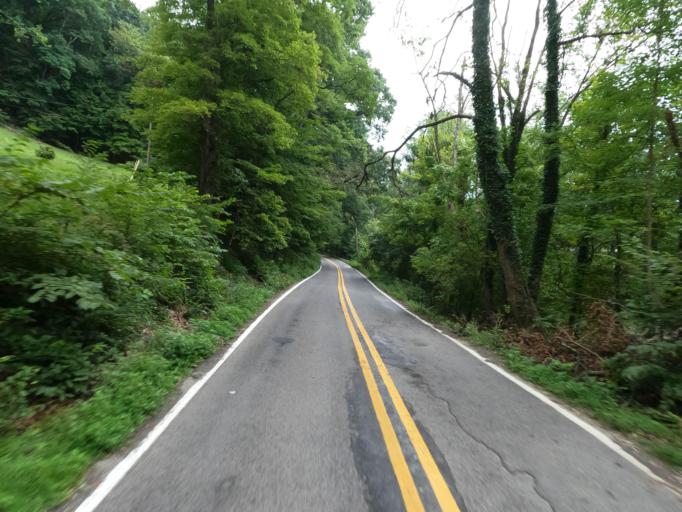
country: US
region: West Virginia
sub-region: Marion County
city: Fairmont
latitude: 39.4998
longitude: -80.0966
